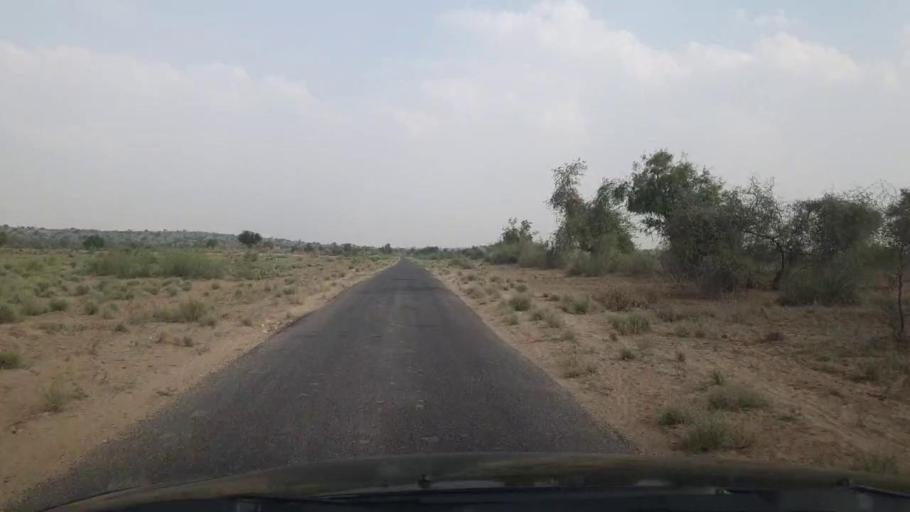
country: PK
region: Sindh
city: Islamkot
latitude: 25.0136
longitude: 70.6332
